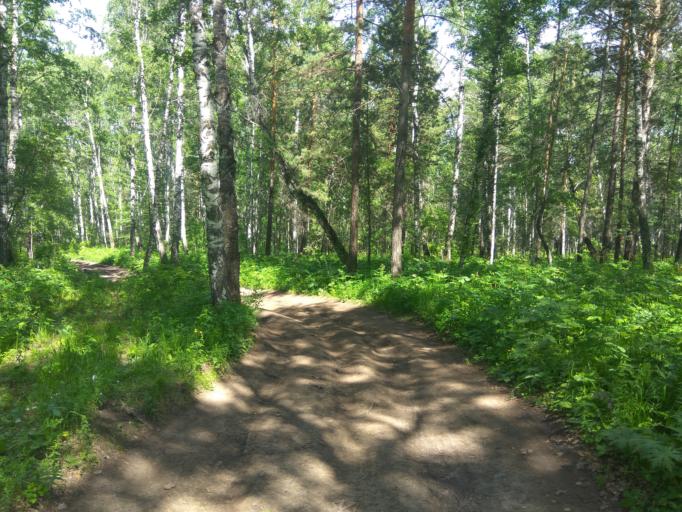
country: RU
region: Krasnoyarskiy
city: Krasnoyarsk
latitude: 55.9508
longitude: 92.8689
